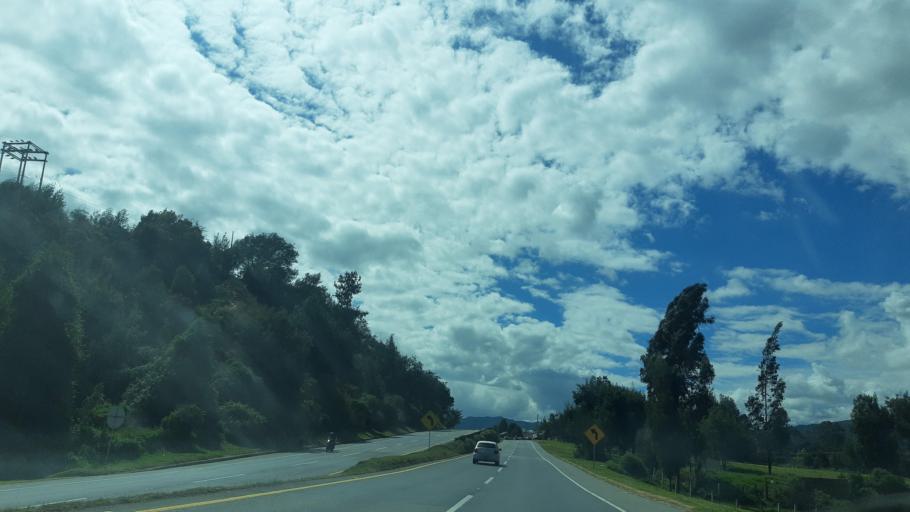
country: CO
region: Cundinamarca
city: Sesquile
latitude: 5.0554
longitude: -73.8034
